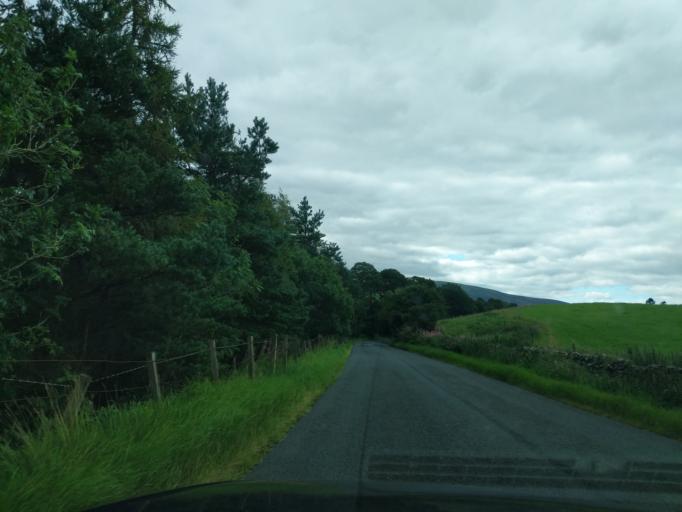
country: GB
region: Scotland
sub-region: The Scottish Borders
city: Peebles
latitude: 55.6385
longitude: -3.2830
